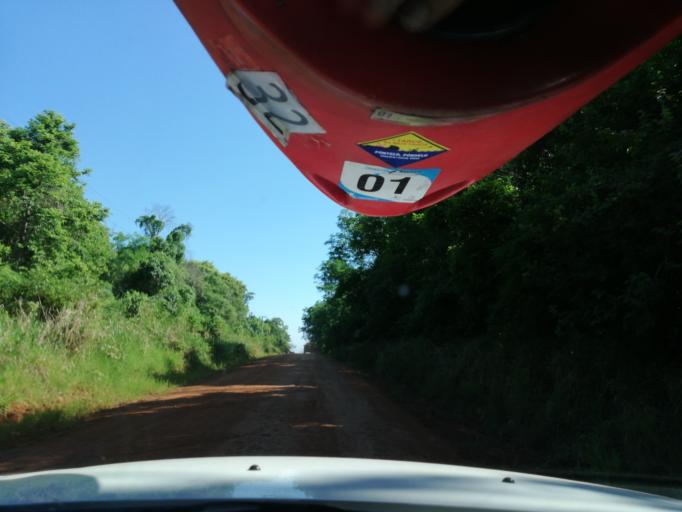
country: AR
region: Misiones
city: Puerto Leoni
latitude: -26.9770
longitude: -55.1647
